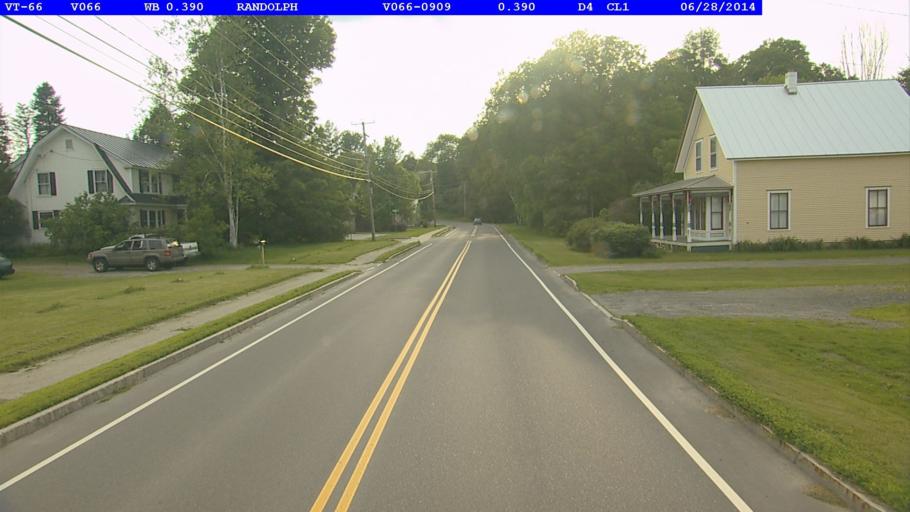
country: US
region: Vermont
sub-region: Orange County
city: Randolph
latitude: 43.9286
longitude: -72.6561
